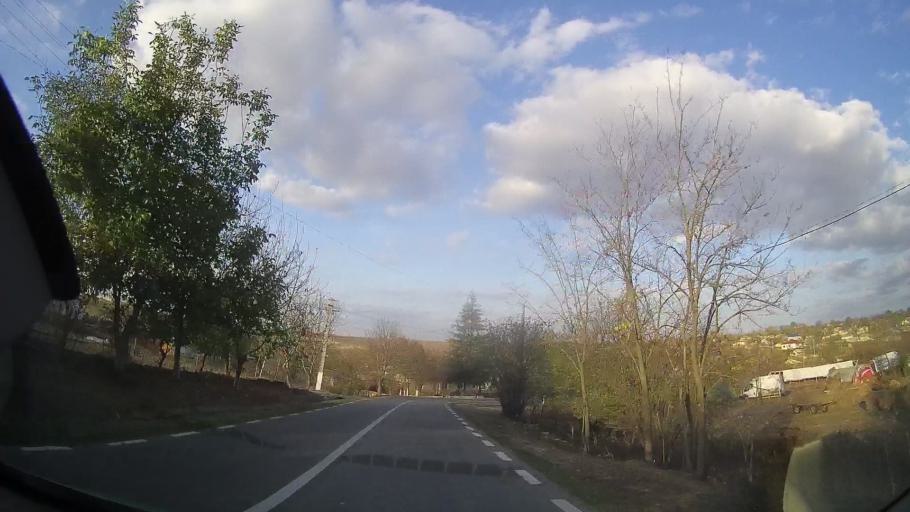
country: RO
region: Constanta
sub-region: Comuna Independenta
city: Independenta
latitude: 43.9532
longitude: 28.0752
